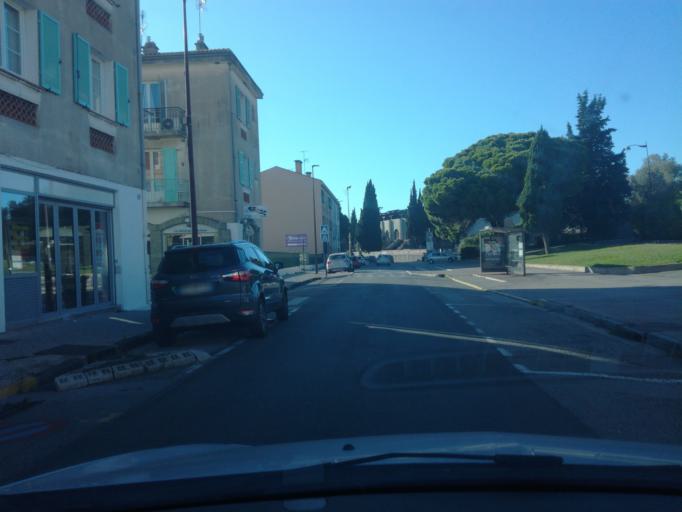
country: FR
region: Provence-Alpes-Cote d'Azur
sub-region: Departement du Var
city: Frejus
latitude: 43.4337
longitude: 6.7304
